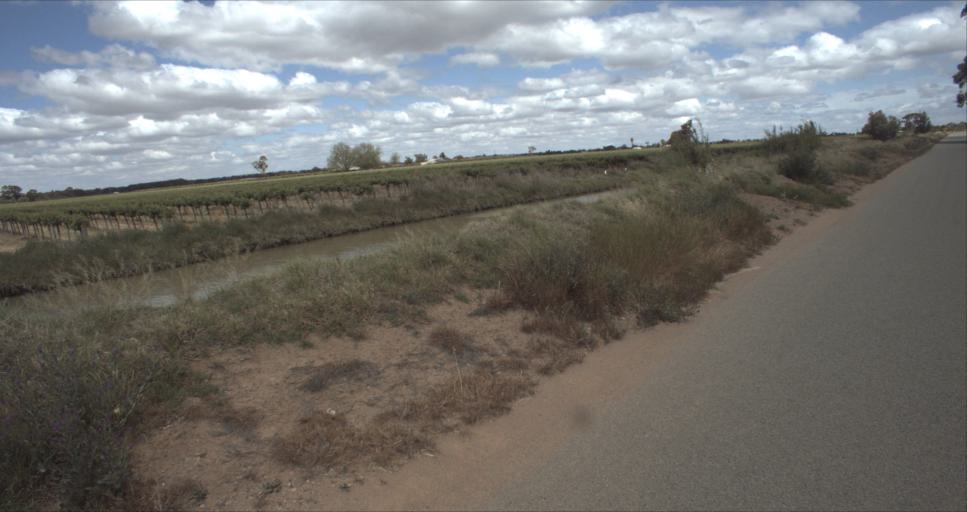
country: AU
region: New South Wales
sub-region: Leeton
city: Leeton
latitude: -34.5746
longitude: 146.3985
